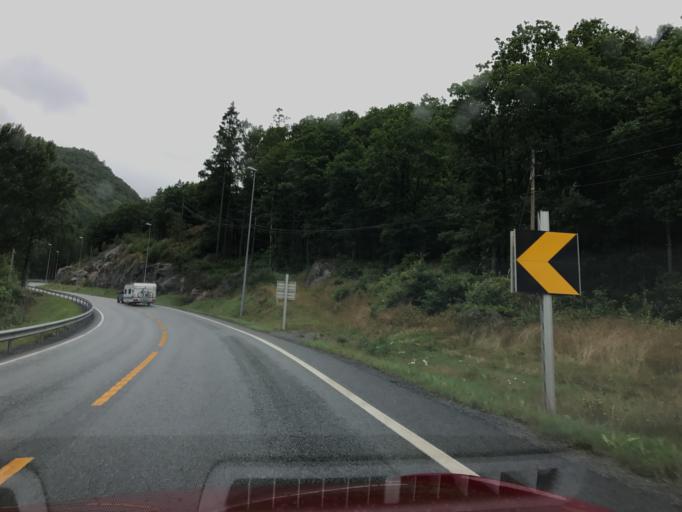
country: NO
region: Vest-Agder
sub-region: Lyngdal
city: Lyngdal
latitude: 58.1365
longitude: 7.1813
